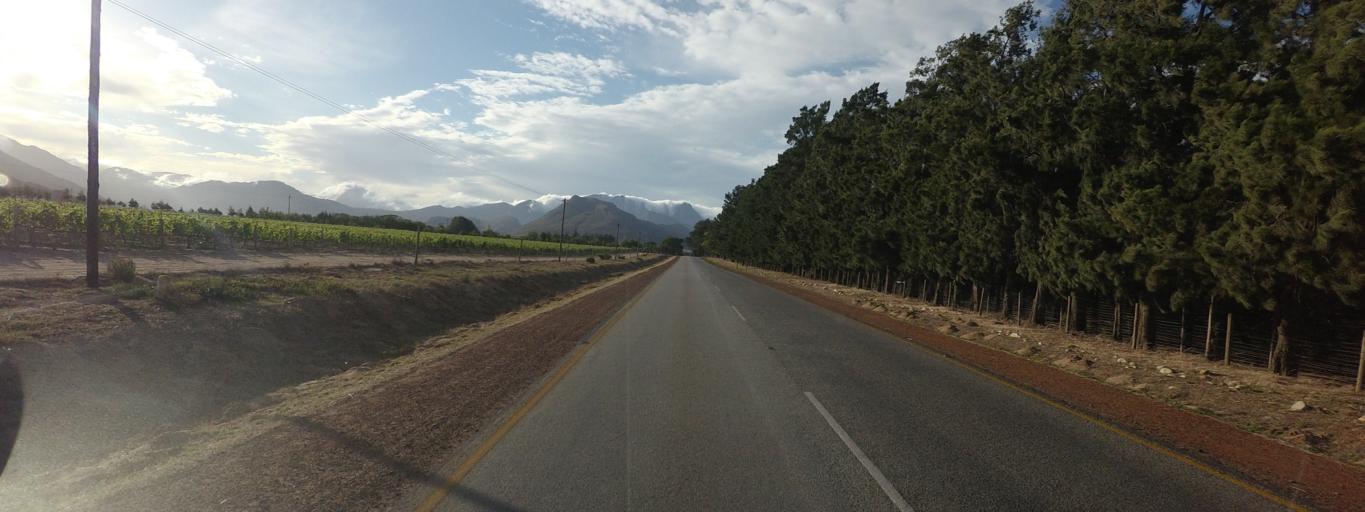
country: ZA
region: Western Cape
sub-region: Cape Winelands District Municipality
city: Paarl
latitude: -33.8666
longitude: 19.0413
